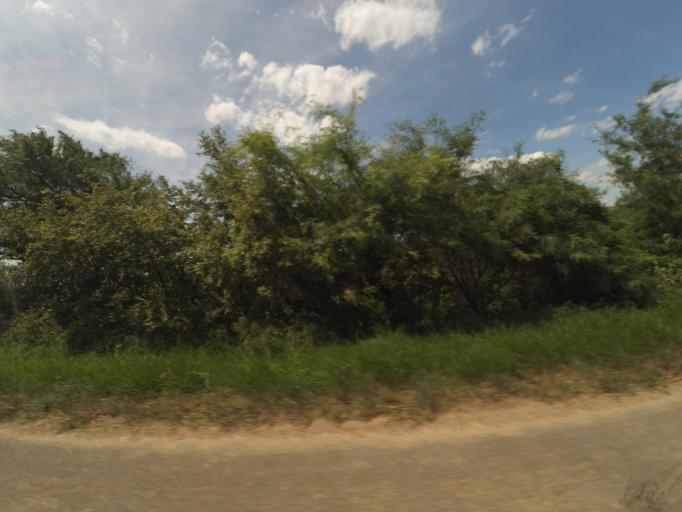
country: BO
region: Santa Cruz
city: Pailon
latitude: -17.5889
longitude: -61.9630
